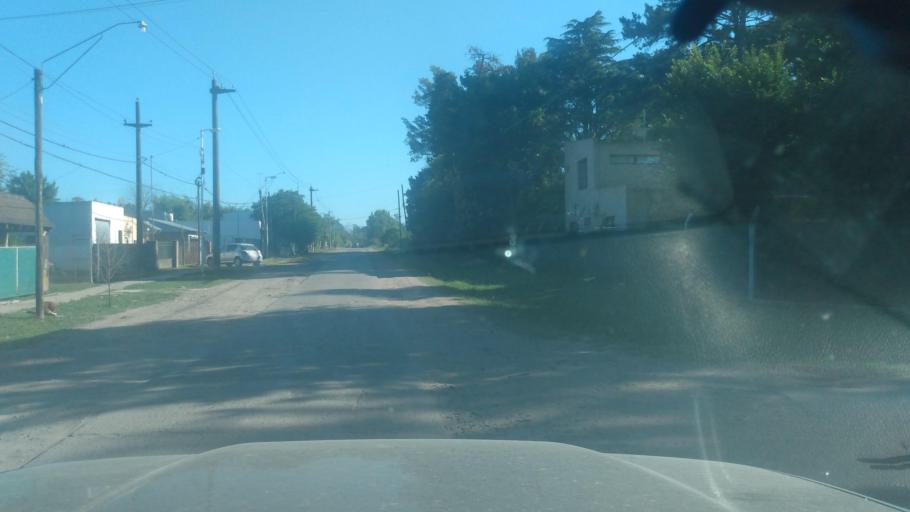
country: AR
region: Buenos Aires
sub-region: Partido de Lujan
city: Lujan
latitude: -34.5880
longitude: -59.0593
